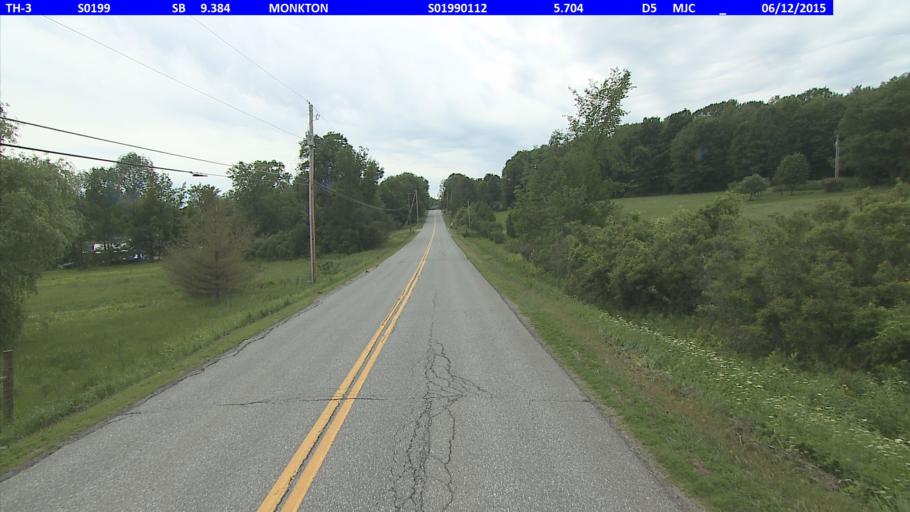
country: US
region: Vermont
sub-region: Chittenden County
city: Hinesburg
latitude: 44.2611
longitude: -73.1211
